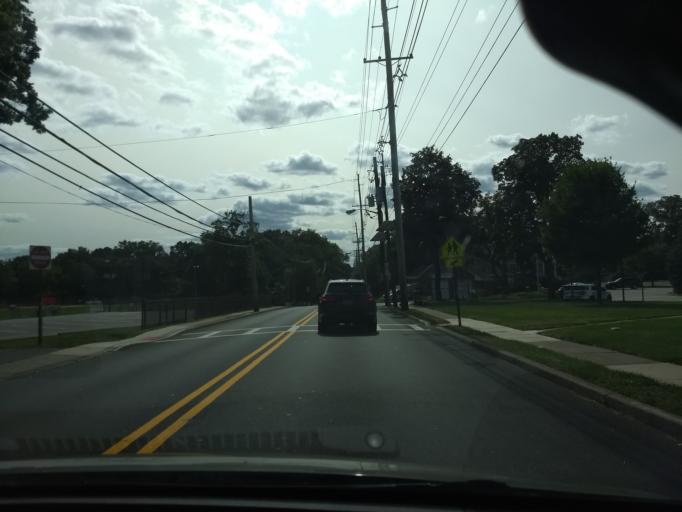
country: US
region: New Jersey
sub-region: Bergen County
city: Glen Rock
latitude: 40.9615
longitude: -74.1272
